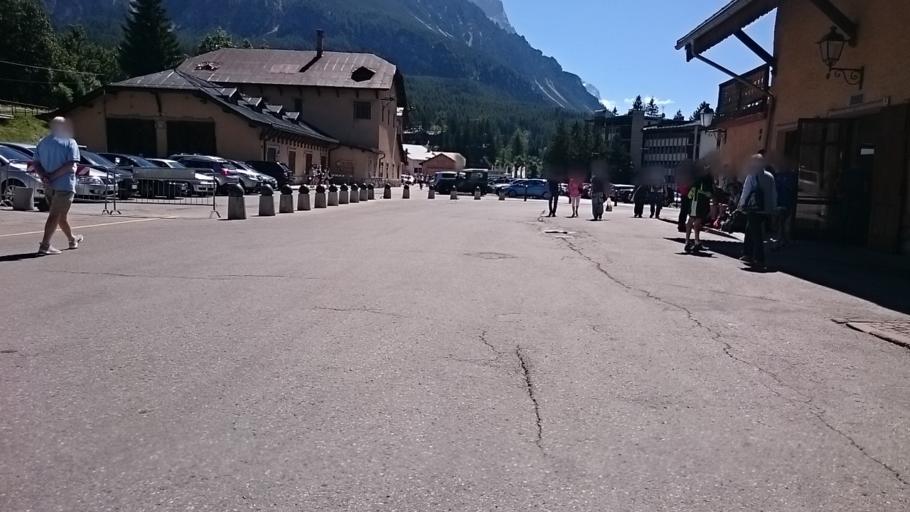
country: IT
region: Veneto
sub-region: Provincia di Belluno
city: Cortina d'Ampezzo
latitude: 46.5391
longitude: 12.1383
